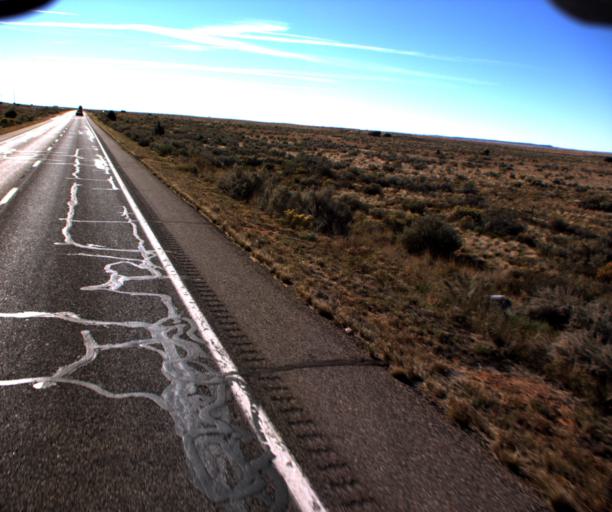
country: US
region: Arizona
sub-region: Mohave County
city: Colorado City
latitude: 36.9000
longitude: -112.9189
